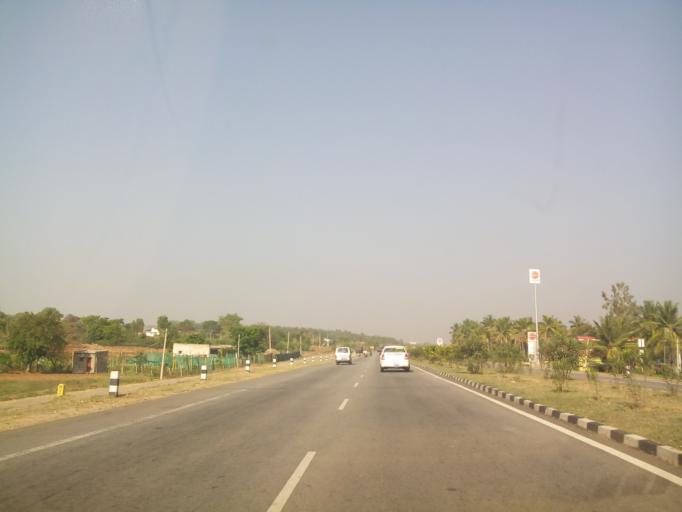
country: IN
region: Karnataka
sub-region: Bangalore Rural
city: Nelamangala
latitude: 13.0663
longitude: 77.3172
